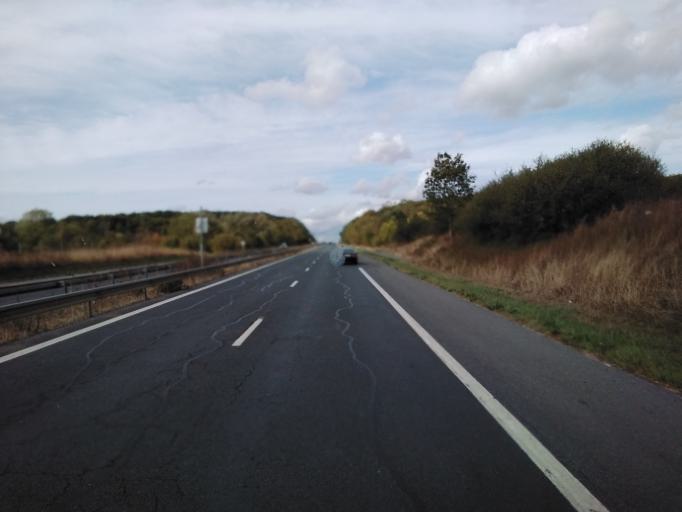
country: FR
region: Champagne-Ardenne
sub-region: Departement des Ardennes
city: Vivier-au-Court
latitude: 49.7306
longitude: 4.8085
